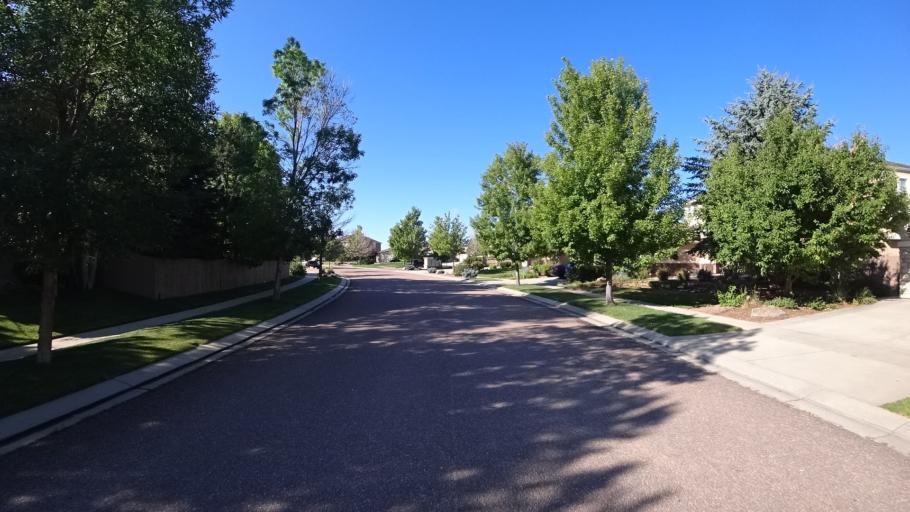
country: US
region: Colorado
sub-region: El Paso County
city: Black Forest
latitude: 38.9816
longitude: -104.7640
